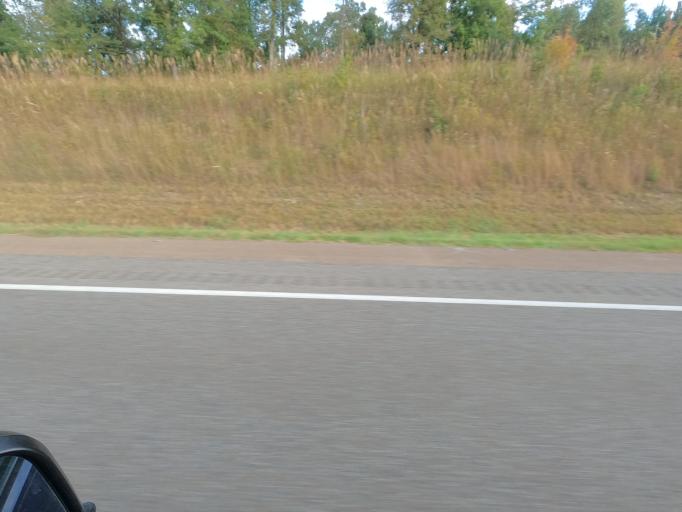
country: US
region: Tennessee
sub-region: Humphreys County
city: New Johnsonville
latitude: 35.8618
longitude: -88.0461
